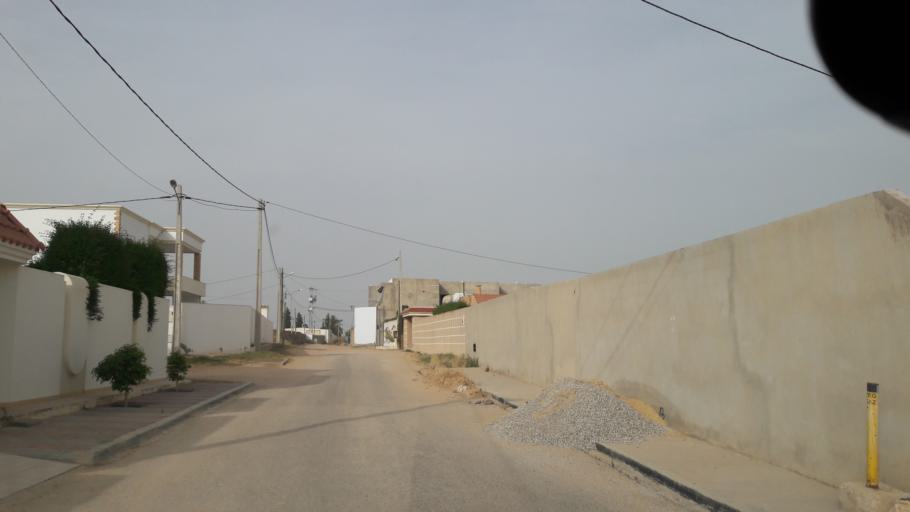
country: TN
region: Safaqis
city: Al Qarmadah
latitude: 34.7801
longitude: 10.7680
